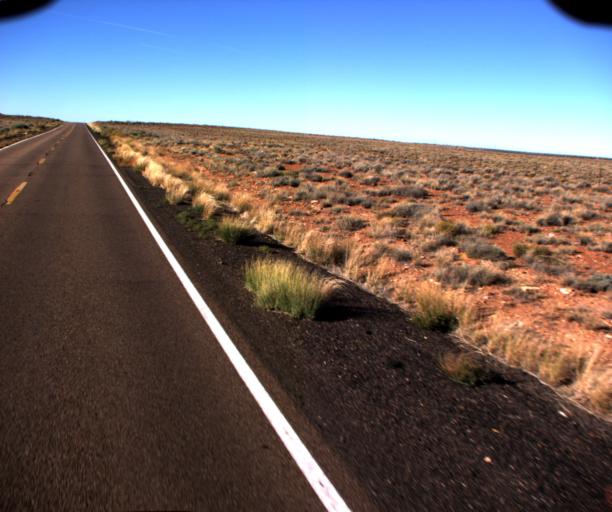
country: US
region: Arizona
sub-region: Navajo County
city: Holbrook
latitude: 34.8402
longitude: -110.1814
